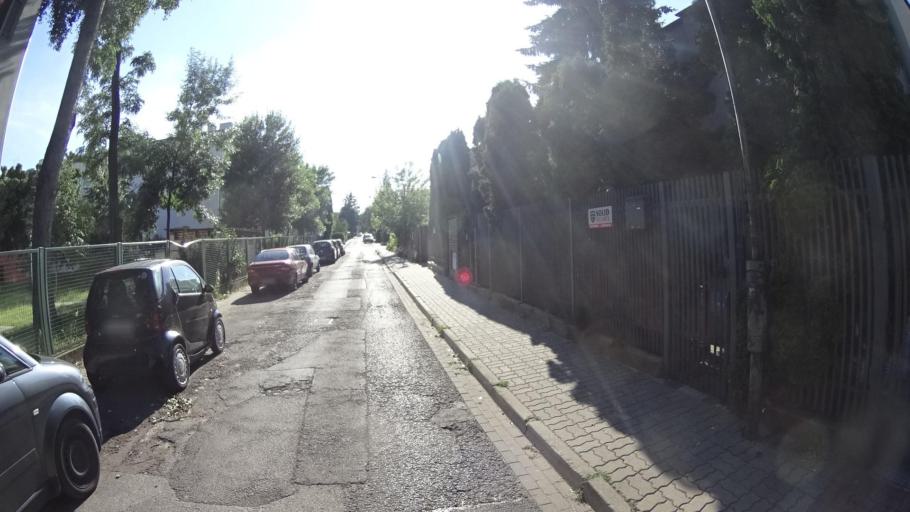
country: PL
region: Masovian Voivodeship
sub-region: Warszawa
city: Bemowo
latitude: 52.2479
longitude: 20.9485
